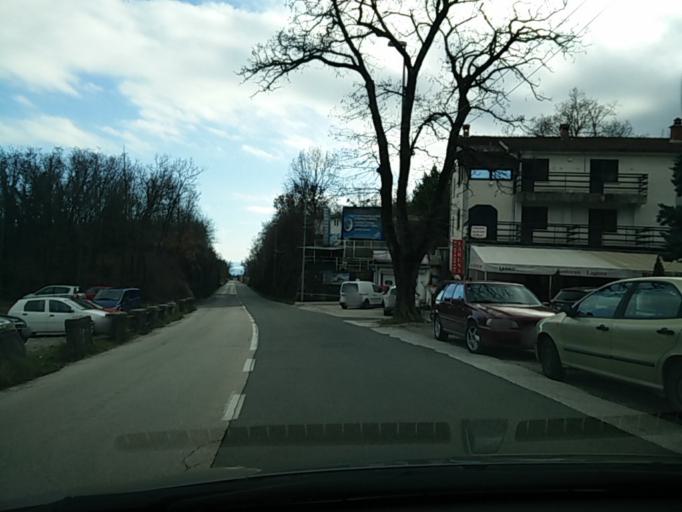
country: HR
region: Primorsko-Goranska
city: Matulji
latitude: 45.3696
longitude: 14.3101
